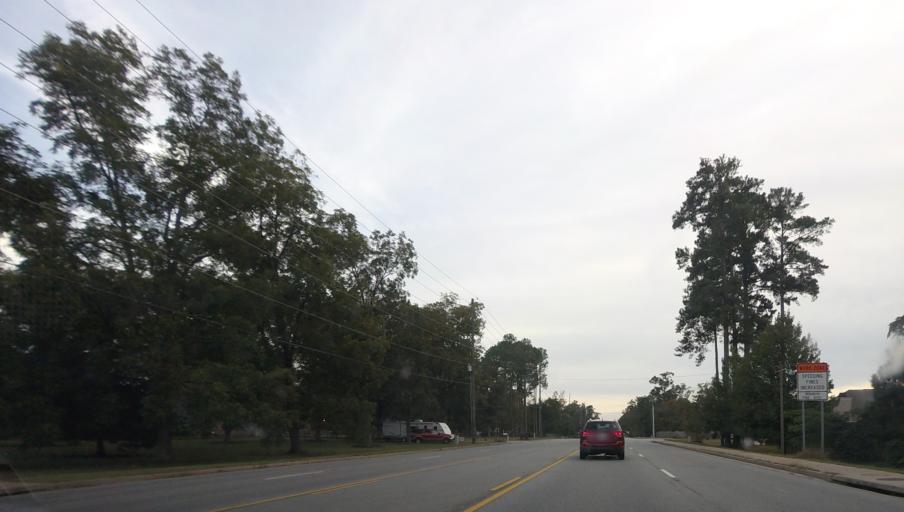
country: US
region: Georgia
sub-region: Houston County
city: Centerville
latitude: 32.5587
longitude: -83.6912
